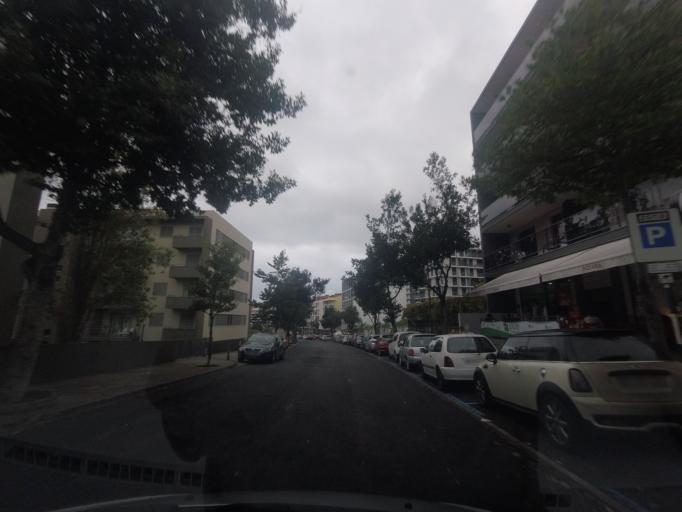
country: PT
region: Madeira
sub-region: Funchal
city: Funchal
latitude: 32.6495
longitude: -16.9299
